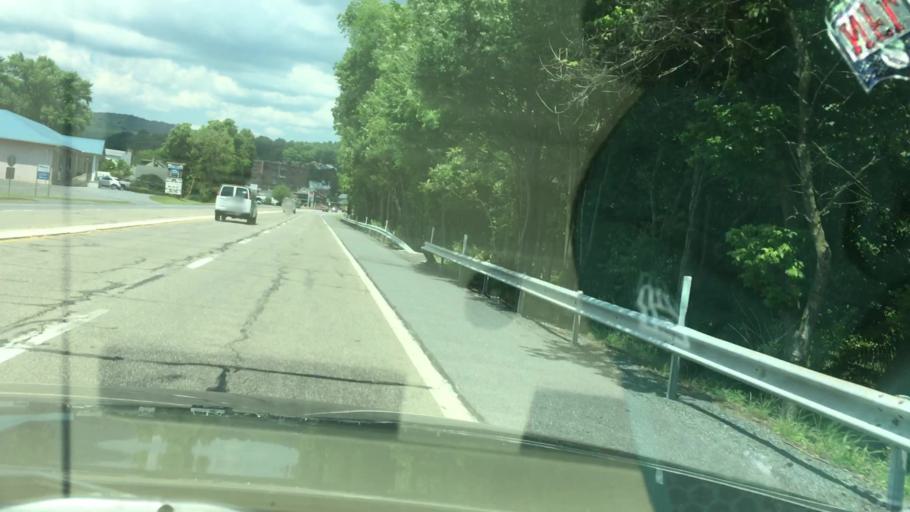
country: US
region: Pennsylvania
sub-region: Schuylkill County
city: Minersville
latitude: 40.6863
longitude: -76.2558
